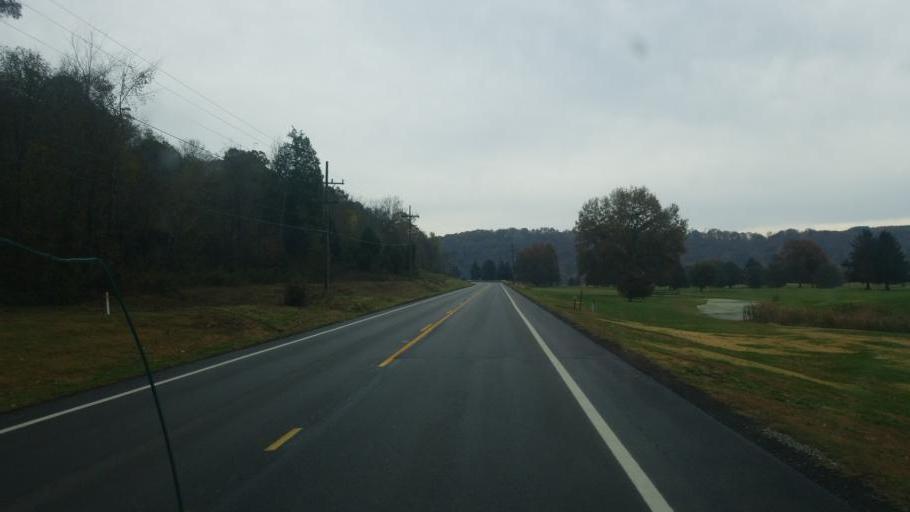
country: US
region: Ohio
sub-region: Washington County
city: Beverly
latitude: 39.5494
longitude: -81.5995
